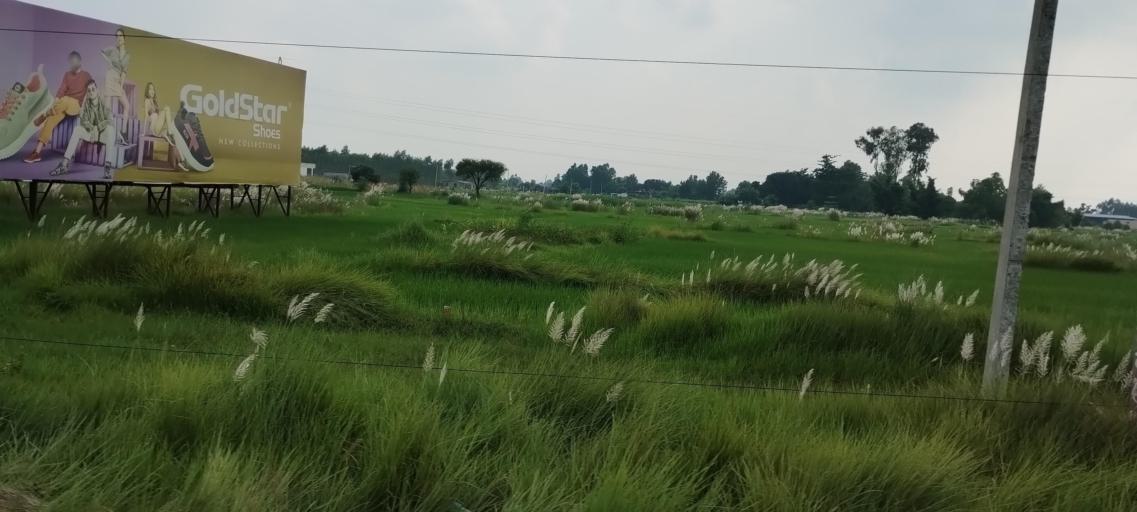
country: NP
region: Mid Western
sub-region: Bheri Zone
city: Nepalgunj
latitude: 28.1987
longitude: 81.6380
